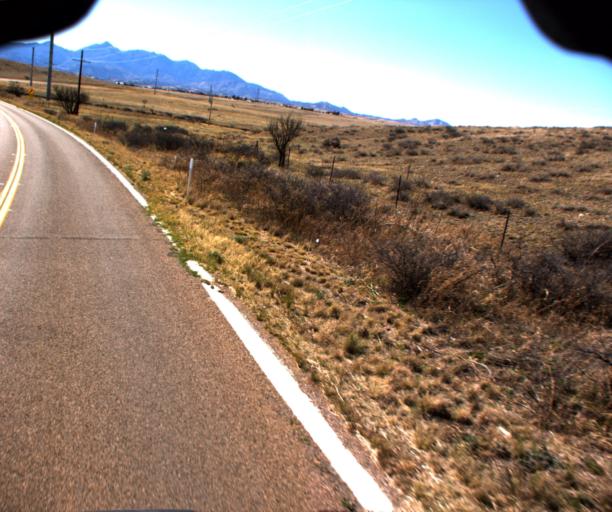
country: US
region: Arizona
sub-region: Cochise County
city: Huachuca City
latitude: 31.6738
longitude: -110.6322
